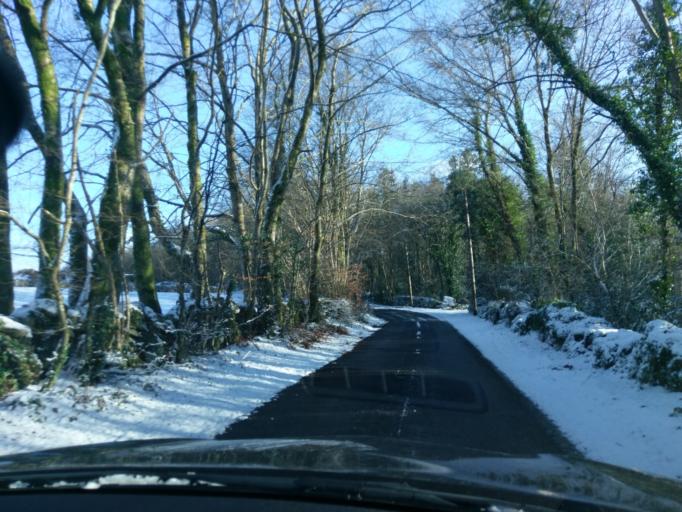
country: IE
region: Connaught
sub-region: County Galway
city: Gort
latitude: 53.1807
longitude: -8.8046
